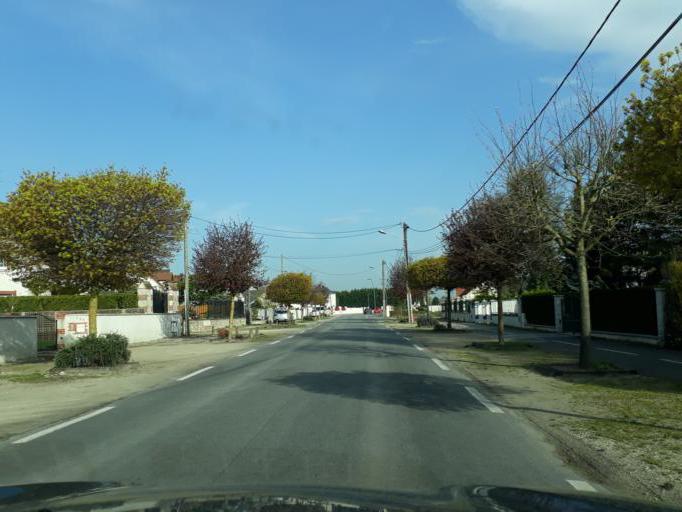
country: FR
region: Centre
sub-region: Departement du Loiret
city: Ingre
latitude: 47.9080
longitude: 1.8335
